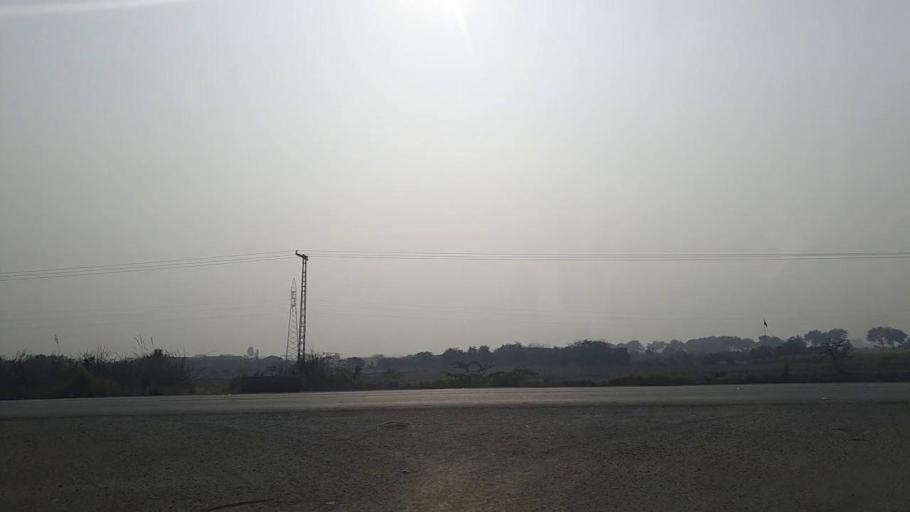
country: PK
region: Sindh
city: Sanghar
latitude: 26.0752
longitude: 68.9173
